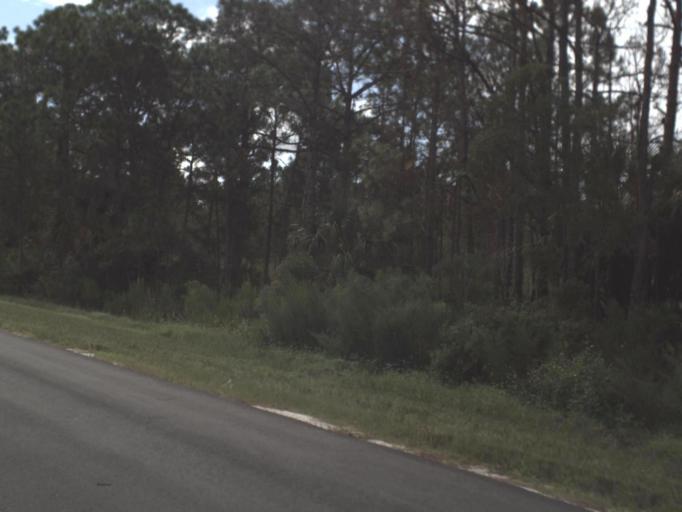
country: US
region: Florida
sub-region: Sarasota County
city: Warm Mineral Springs
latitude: 27.1004
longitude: -82.2844
